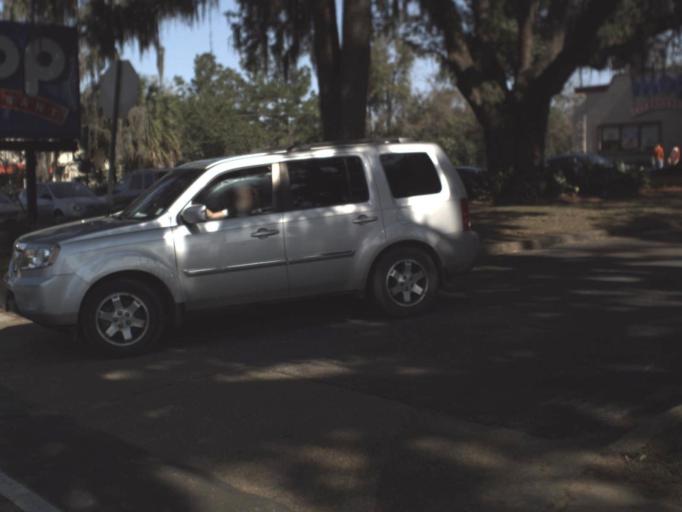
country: US
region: Florida
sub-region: Leon County
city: Tallahassee
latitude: 30.4699
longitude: -84.2882
